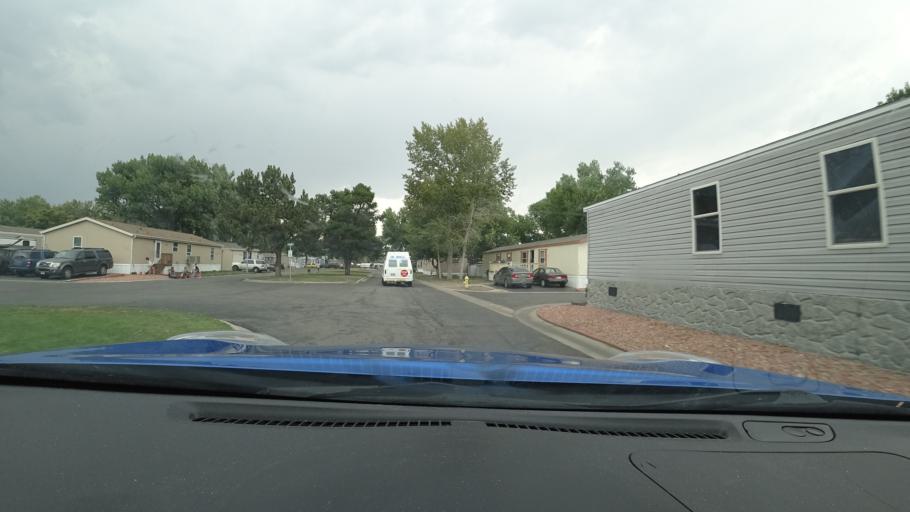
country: US
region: Colorado
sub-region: Adams County
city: Aurora
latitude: 39.7442
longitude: -104.7852
